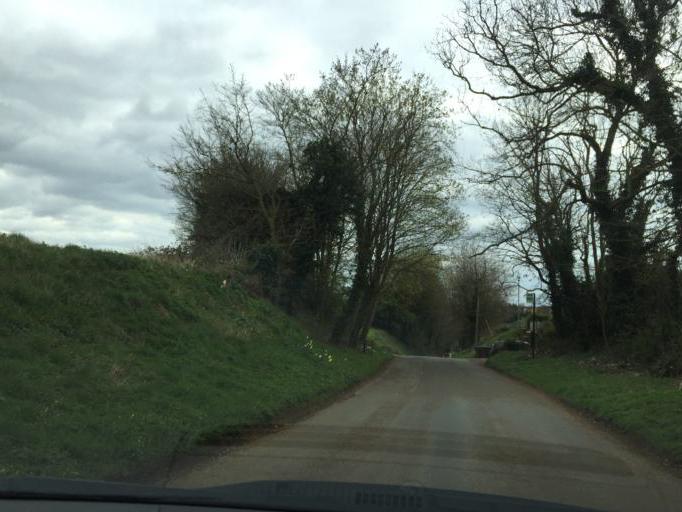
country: GB
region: England
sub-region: Oxfordshire
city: Hanwell
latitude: 52.1055
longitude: -1.4290
